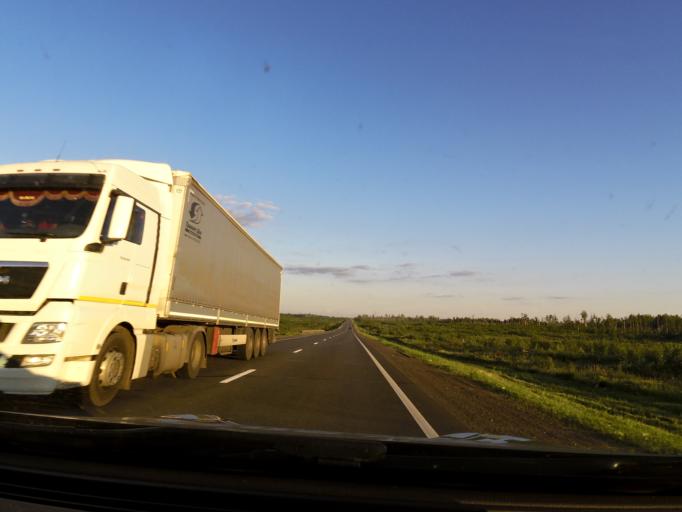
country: RU
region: Jaroslavl
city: Prechistoye
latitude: 58.6164
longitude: 40.3343
